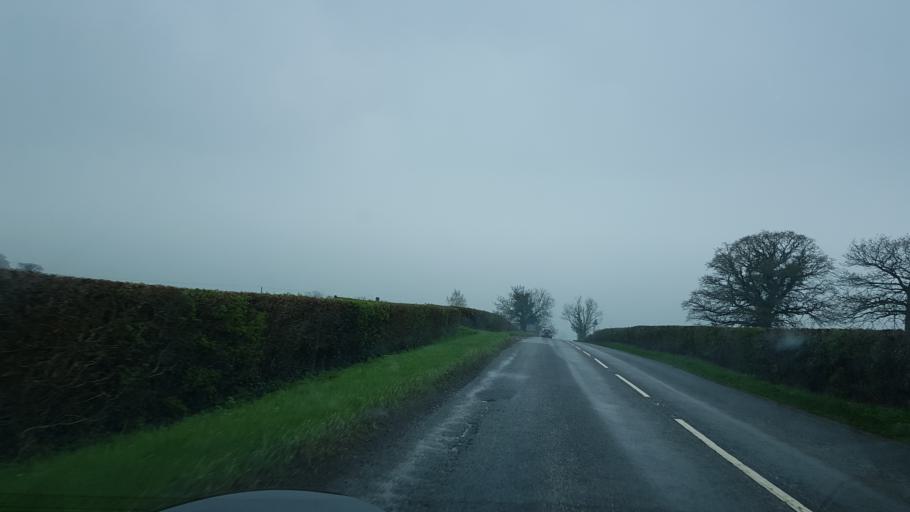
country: GB
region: England
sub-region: Herefordshire
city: Moreton Jeffries
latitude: 52.1356
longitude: -2.5676
